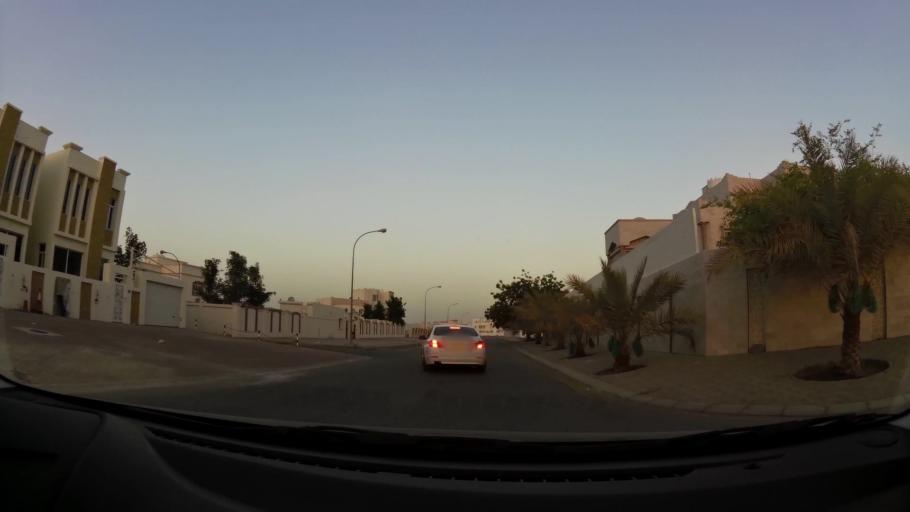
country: OM
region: Muhafazat Masqat
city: As Sib al Jadidah
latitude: 23.6469
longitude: 58.2111
